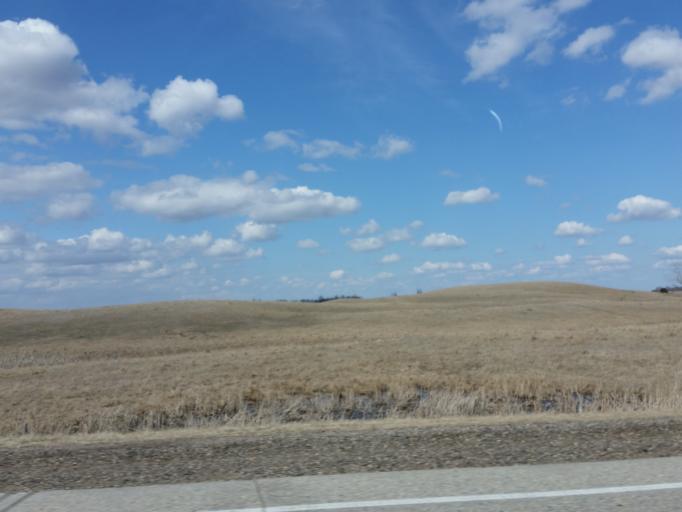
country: US
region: South Dakota
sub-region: Deuel County
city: Clear Lake
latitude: 44.8901
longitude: -96.7223
